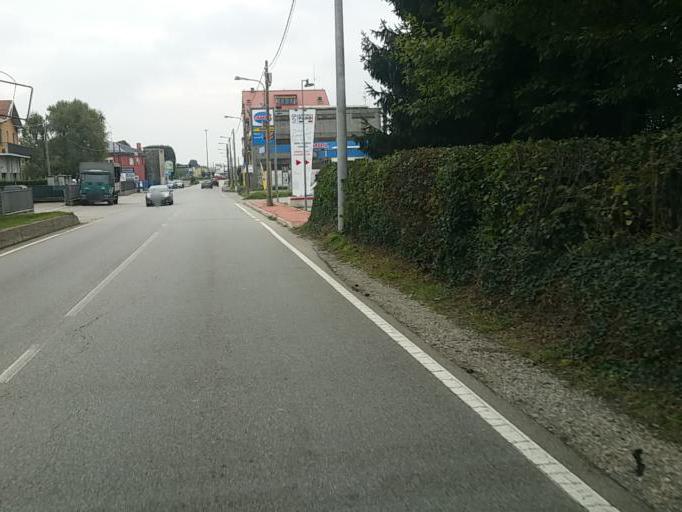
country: IT
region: Piedmont
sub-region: Provincia di Novara
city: Gozzano
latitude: 45.7384
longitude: 8.4391
